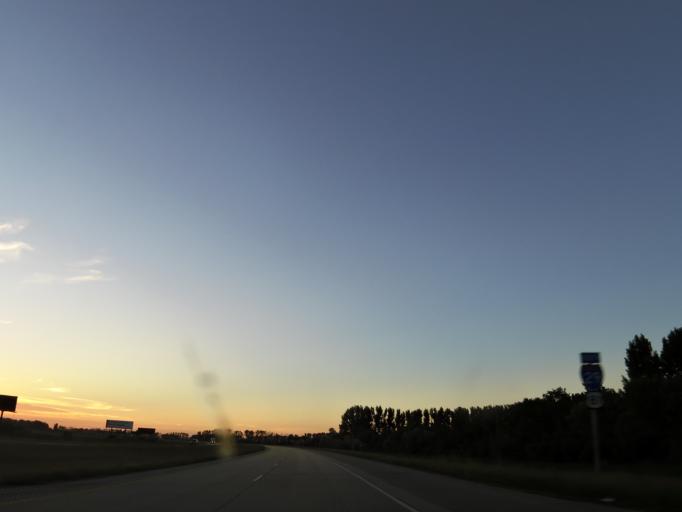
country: US
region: North Dakota
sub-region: Grand Forks County
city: Grand Forks
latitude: 47.9931
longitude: -97.0928
